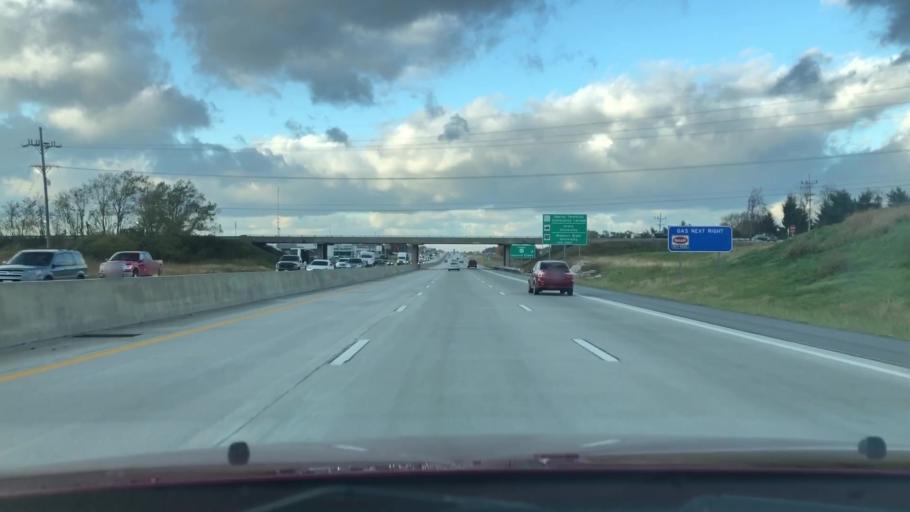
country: US
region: Missouri
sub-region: Greene County
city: Springfield
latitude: 37.2008
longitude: -93.2261
